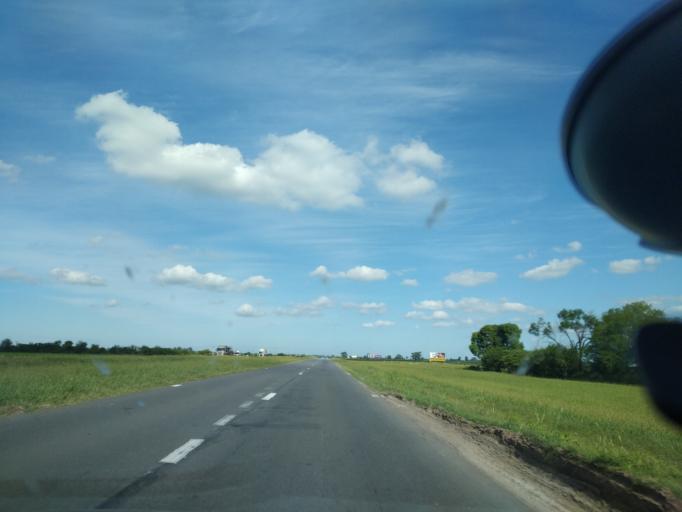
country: AR
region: Santa Fe
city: Roldan
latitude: -32.9124
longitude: -60.9683
